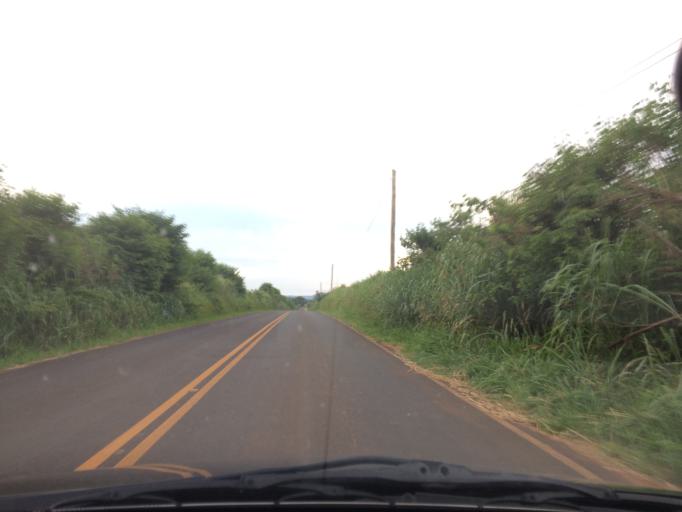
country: BR
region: Sao Paulo
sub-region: Casa Branca
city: Casa Branca
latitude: -21.7596
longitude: -47.1107
